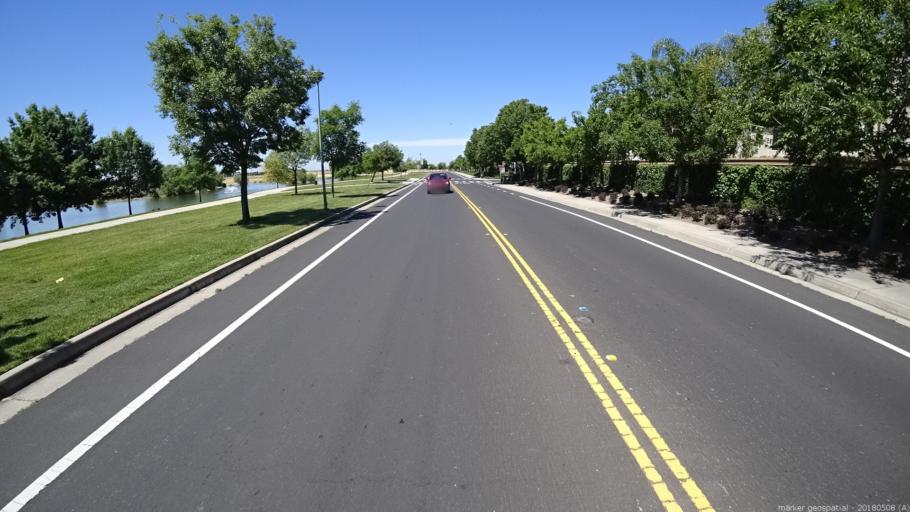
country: US
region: California
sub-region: Sacramento County
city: Rio Linda
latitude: 38.6656
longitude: -121.5099
